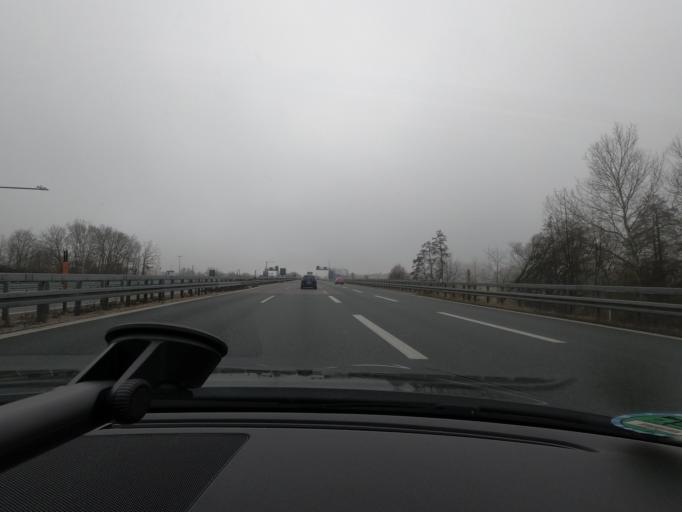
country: DE
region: Bavaria
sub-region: Regierungsbezirk Mittelfranken
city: Erlangen
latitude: 49.6088
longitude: 10.9984
